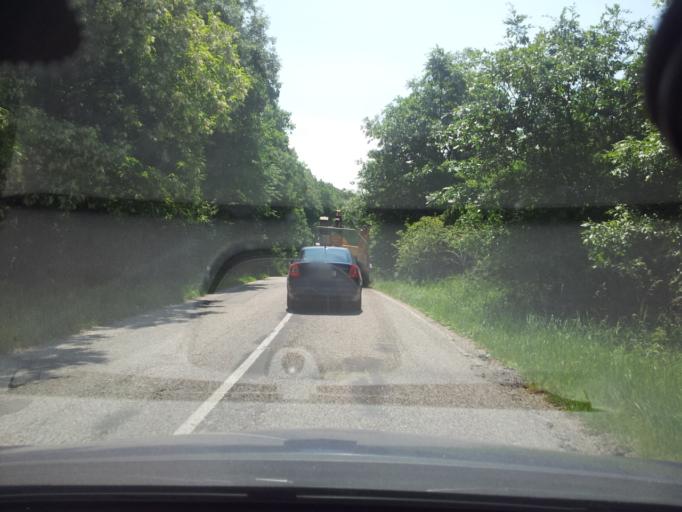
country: SK
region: Nitriansky
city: Partizanske
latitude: 48.5177
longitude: 18.4311
